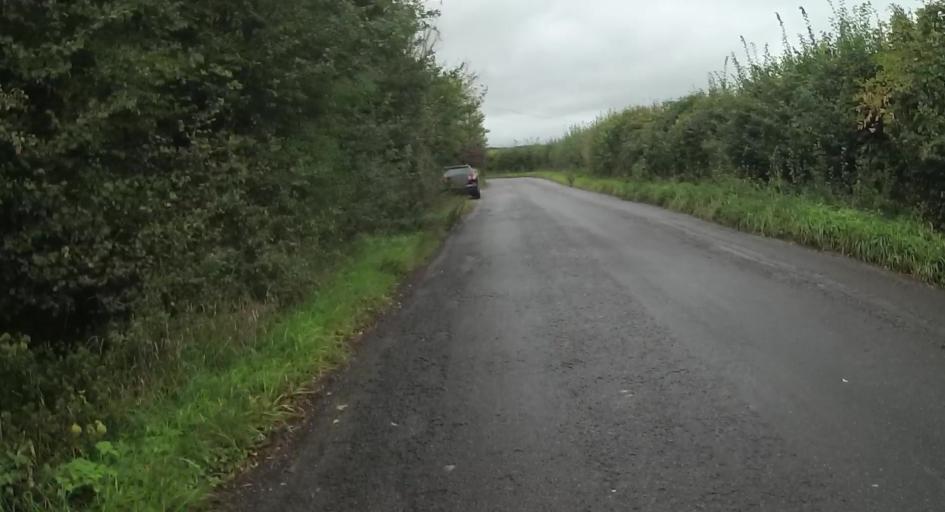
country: GB
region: England
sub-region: Hampshire
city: Tadley
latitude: 51.3894
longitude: -1.1762
